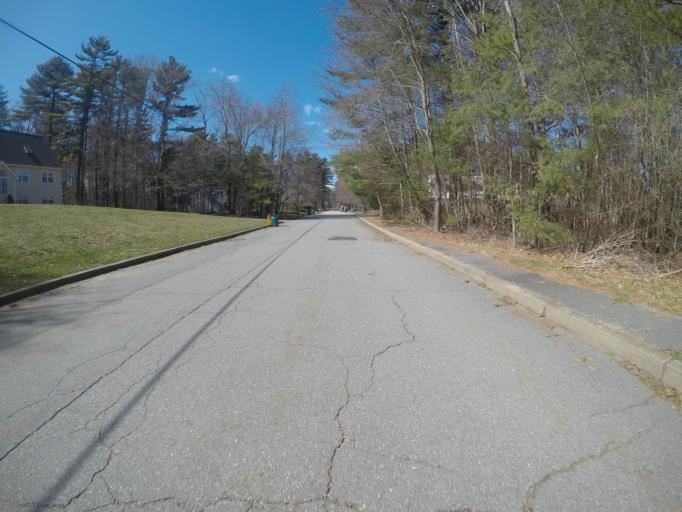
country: US
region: Massachusetts
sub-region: Bristol County
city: Easton
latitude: 42.0065
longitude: -71.1056
